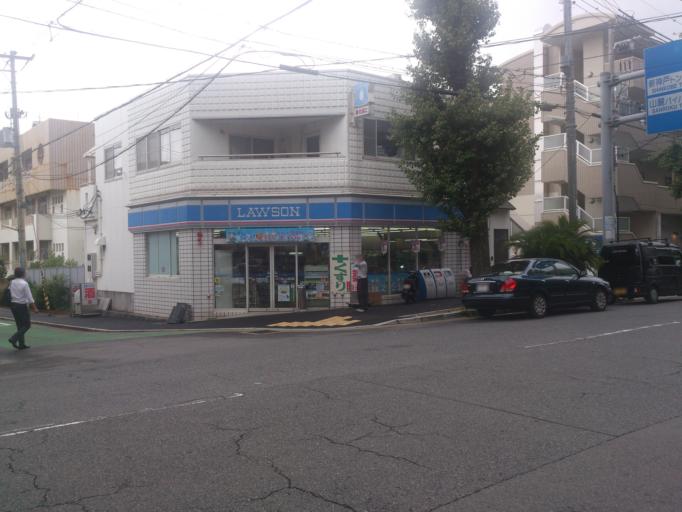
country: JP
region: Hyogo
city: Kobe
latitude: 34.7030
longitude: 135.1996
